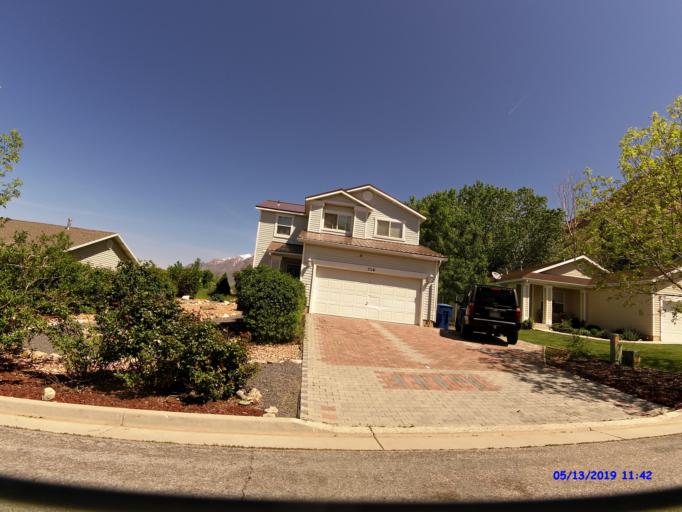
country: US
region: Utah
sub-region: Weber County
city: North Ogden
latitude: 41.2763
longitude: -111.9498
